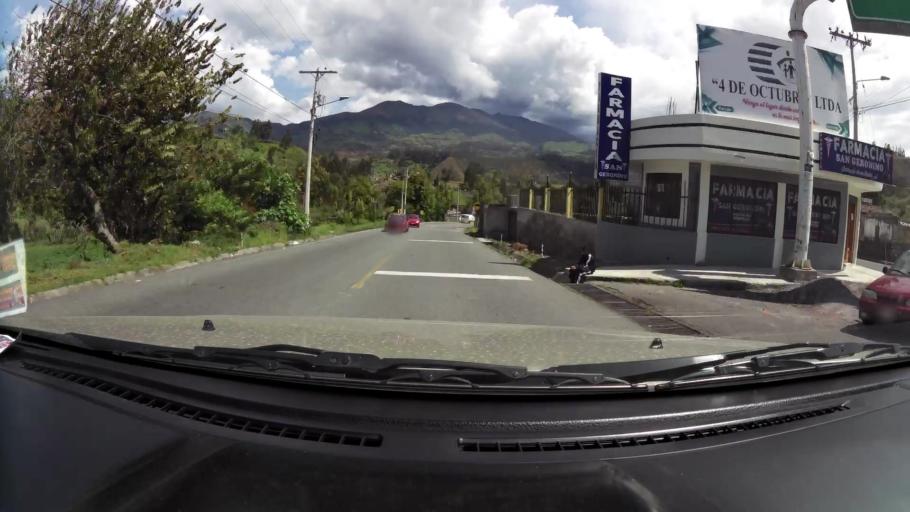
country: EC
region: Chimborazo
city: Guano
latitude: -1.6392
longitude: -78.5886
